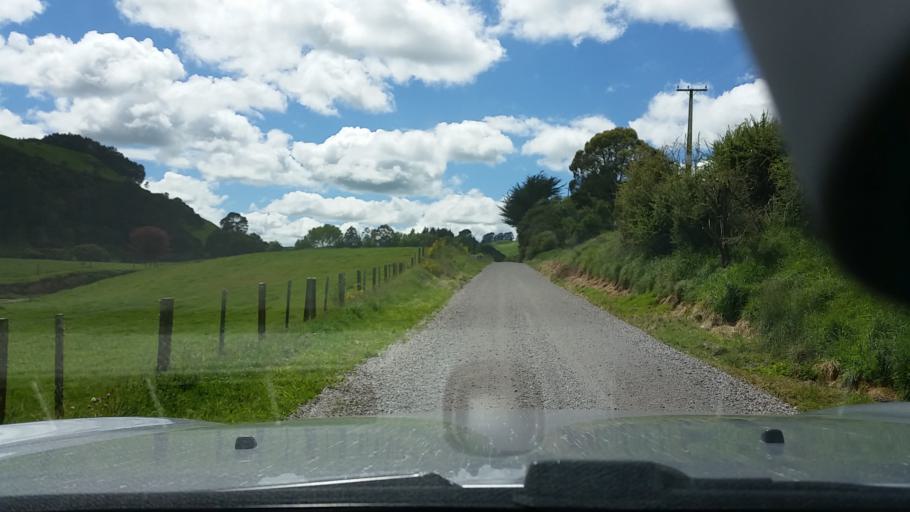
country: NZ
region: Waikato
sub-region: South Waikato District
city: Tokoroa
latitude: -38.3645
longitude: 176.0602
